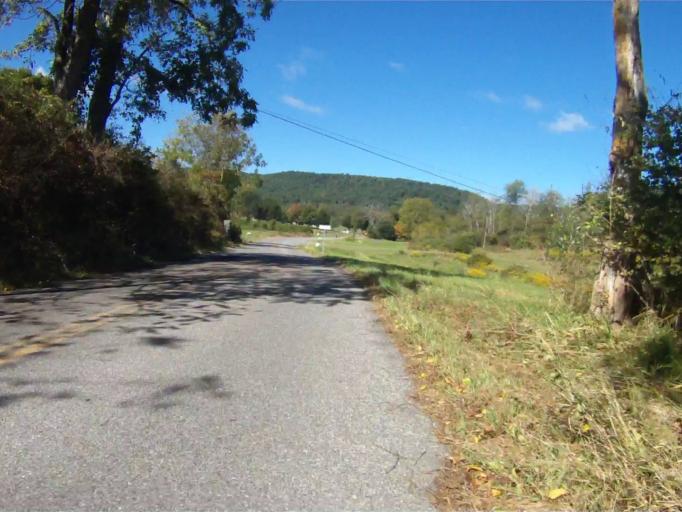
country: US
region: Pennsylvania
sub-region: Centre County
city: Houserville
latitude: 40.8622
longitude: -77.8812
